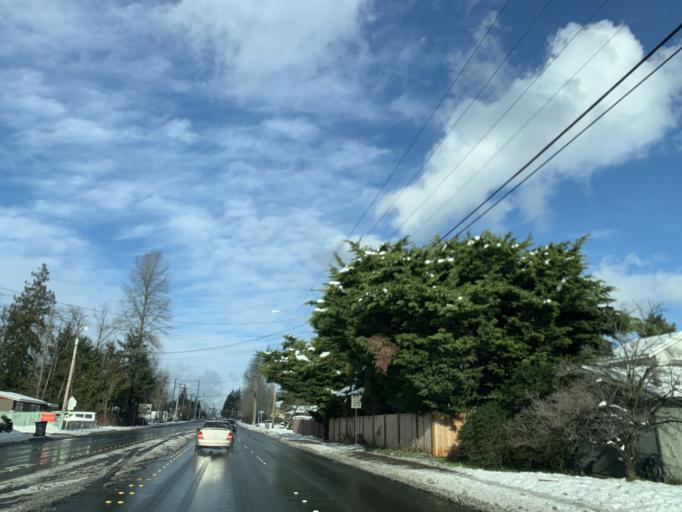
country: US
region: Washington
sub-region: Snohomish County
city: Martha Lake
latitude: 47.8934
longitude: -122.2388
